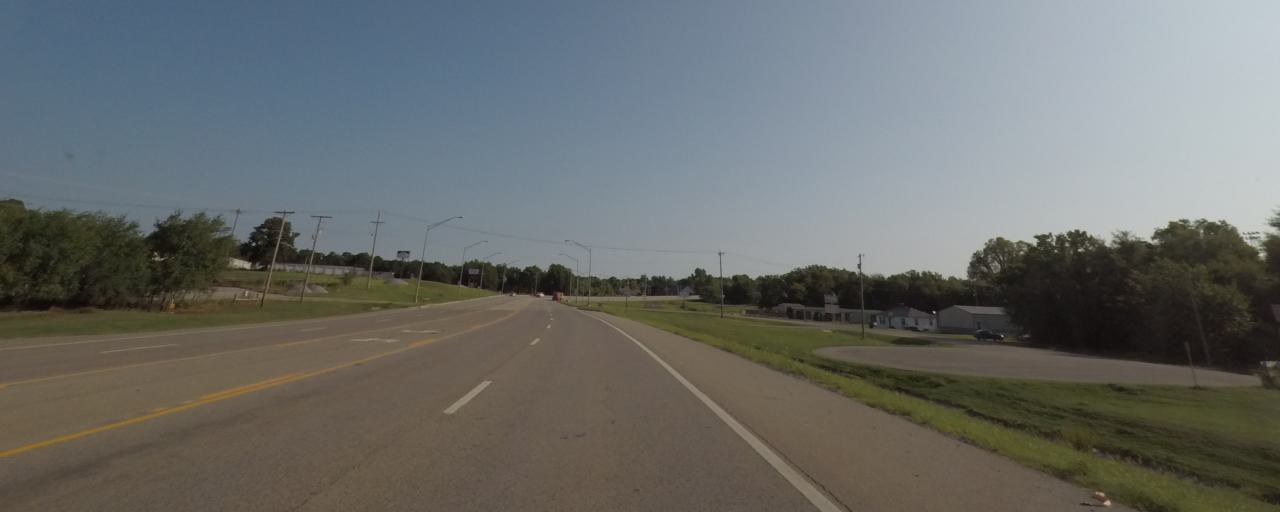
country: US
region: Oklahoma
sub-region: McClain County
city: Blanchard
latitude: 35.1338
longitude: -97.6648
